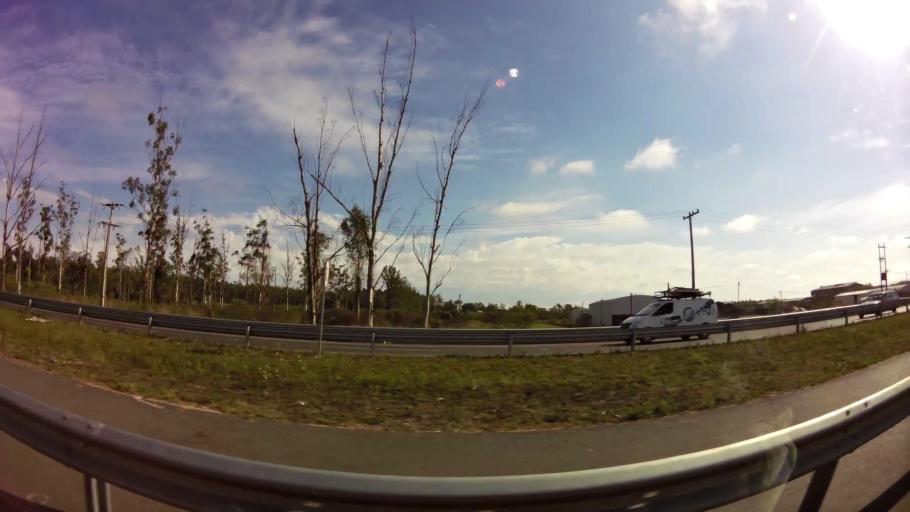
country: PY
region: Central
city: Fernando de la Mora
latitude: -25.2590
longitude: -57.5376
